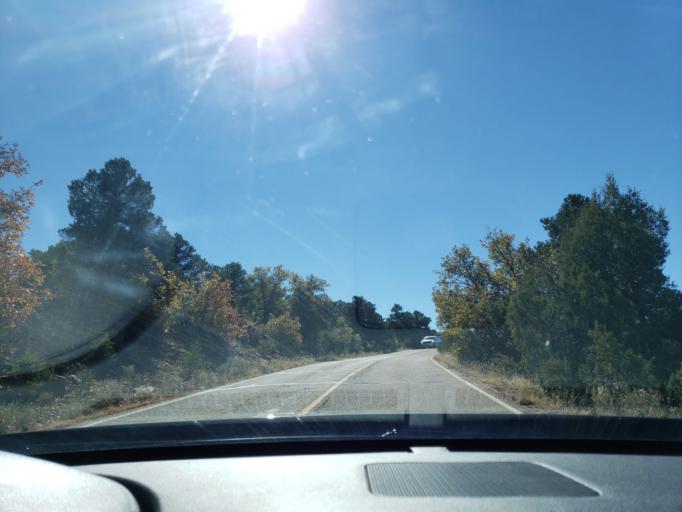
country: US
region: Colorado
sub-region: Fremont County
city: Canon City
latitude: 38.4742
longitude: -105.3073
